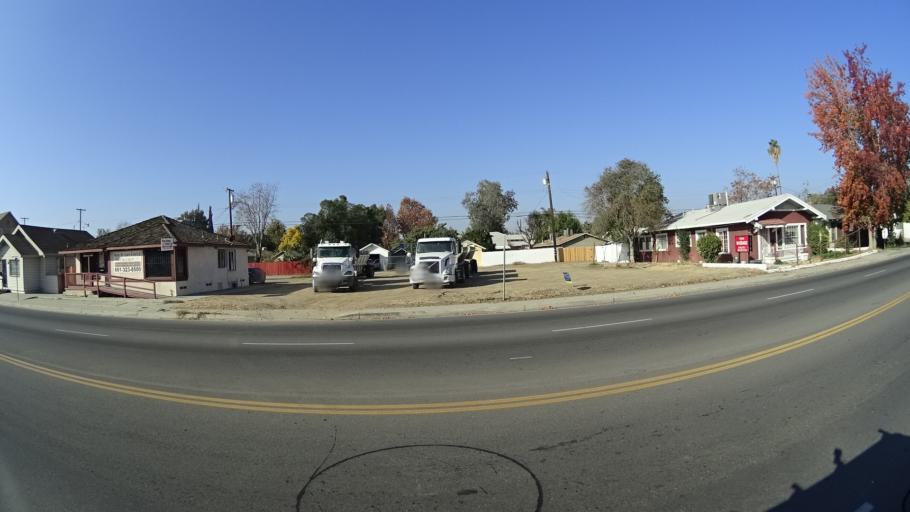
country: US
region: California
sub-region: Kern County
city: Bakersfield
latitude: 35.3605
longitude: -119.0212
